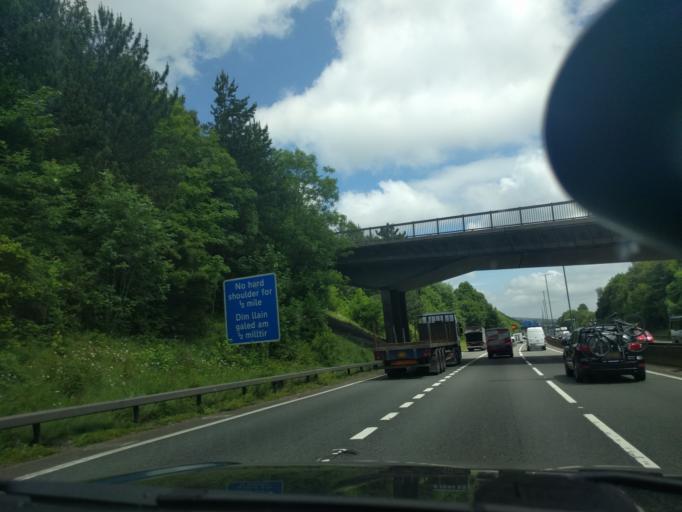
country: GB
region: Wales
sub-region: Newport
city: Caerleon
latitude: 51.5987
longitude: -2.9403
